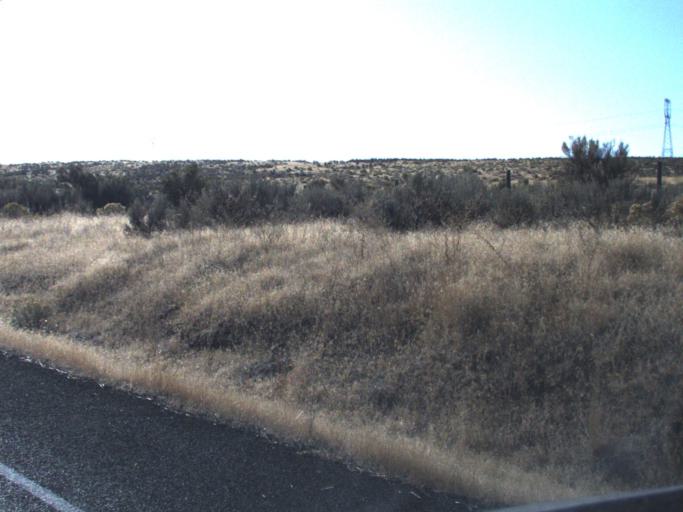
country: US
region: Washington
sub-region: Franklin County
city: Connell
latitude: 46.6454
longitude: -118.8347
